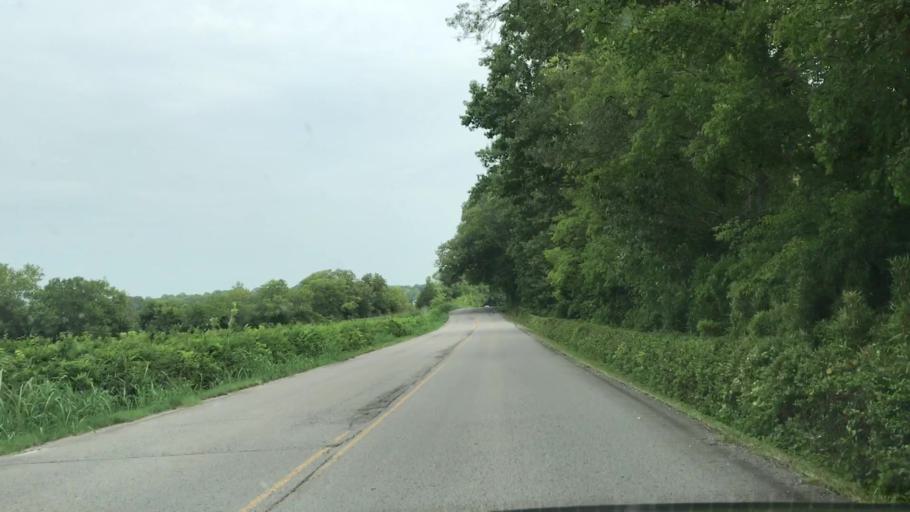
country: US
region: Tennessee
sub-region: Williamson County
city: Nolensville
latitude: 35.9665
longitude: -86.6333
